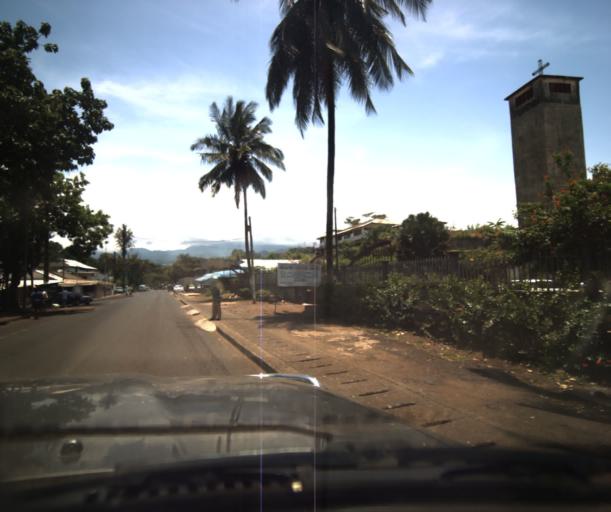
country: CM
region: South-West Province
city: Limbe
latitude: 4.0089
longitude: 9.2084
